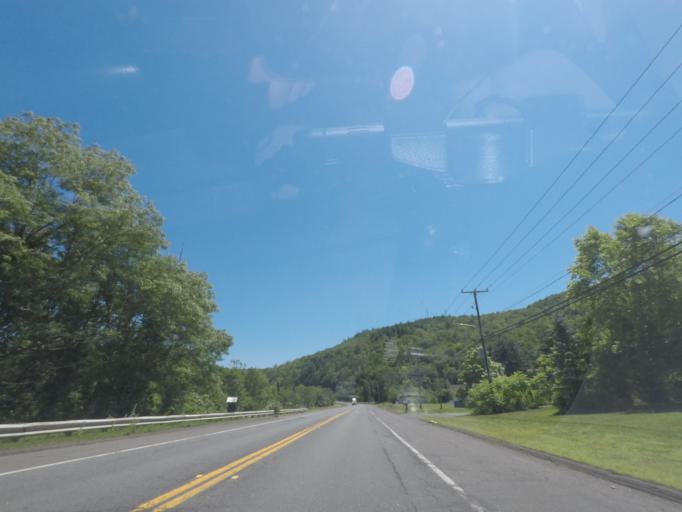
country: US
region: Massachusetts
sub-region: Hampden County
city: Westfield
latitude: 42.1814
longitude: -72.8459
